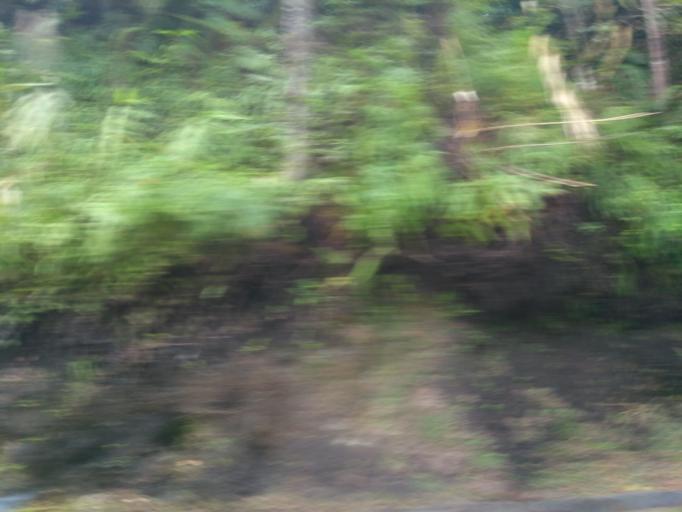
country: MY
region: Pahang
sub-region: Cameron Highlands
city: Tanah Rata
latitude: 4.4646
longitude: 101.3660
